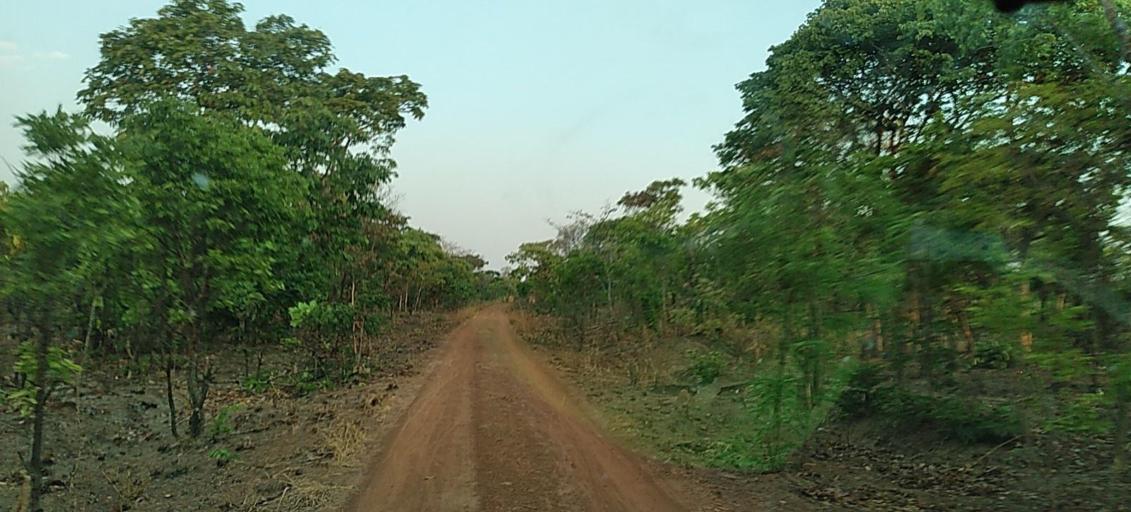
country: ZM
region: North-Western
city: Kalengwa
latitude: -13.1197
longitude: 25.1760
